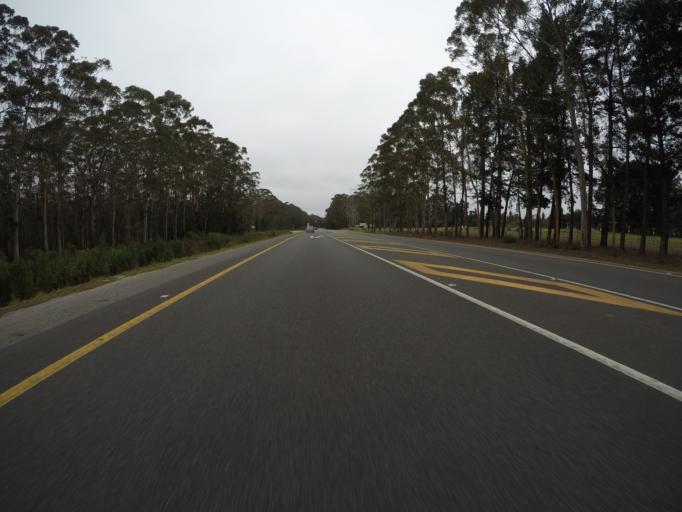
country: ZA
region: Western Cape
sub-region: Eden District Municipality
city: Plettenberg Bay
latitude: -33.9797
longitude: 23.4355
